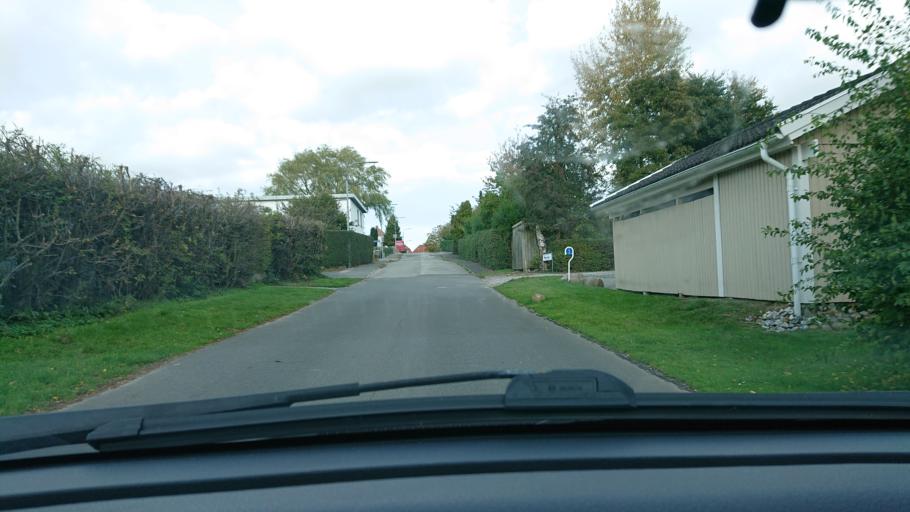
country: DK
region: South Denmark
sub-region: Nyborg Kommune
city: Nyborg
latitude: 55.3073
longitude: 10.7644
